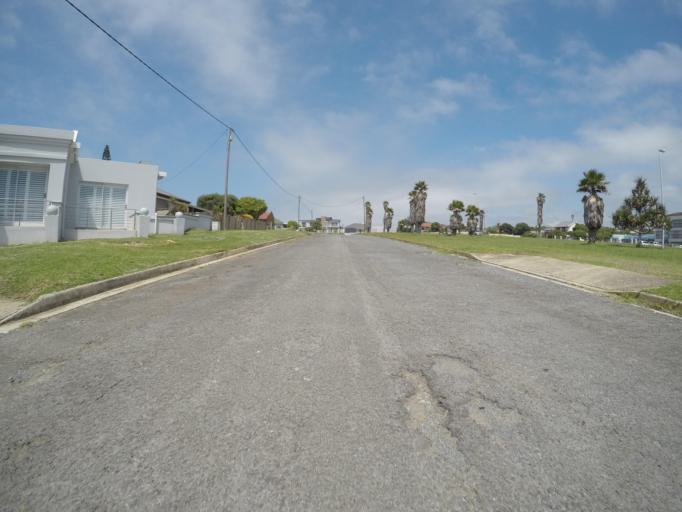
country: ZA
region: Eastern Cape
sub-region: Buffalo City Metropolitan Municipality
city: East London
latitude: -32.9400
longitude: 28.0308
